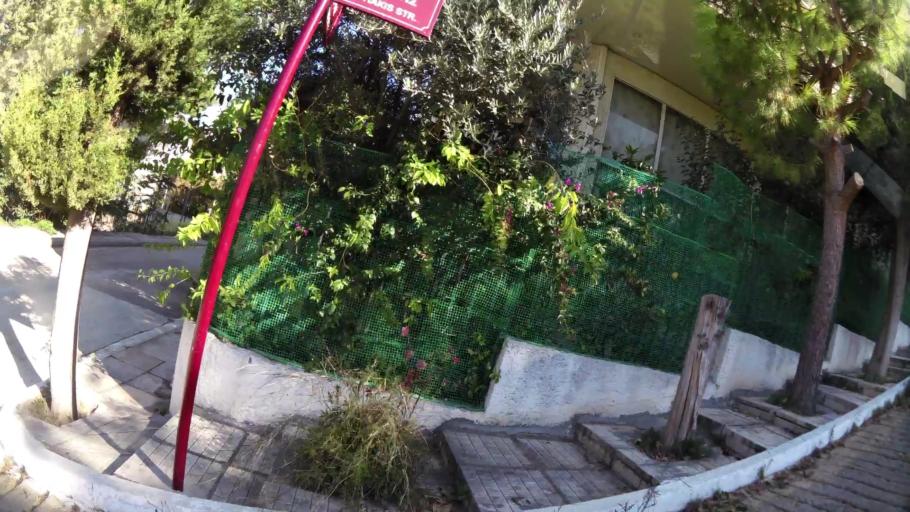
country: GR
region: Attica
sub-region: Nomarchia Athinas
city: Metamorfosi
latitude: 38.0680
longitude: 23.7539
